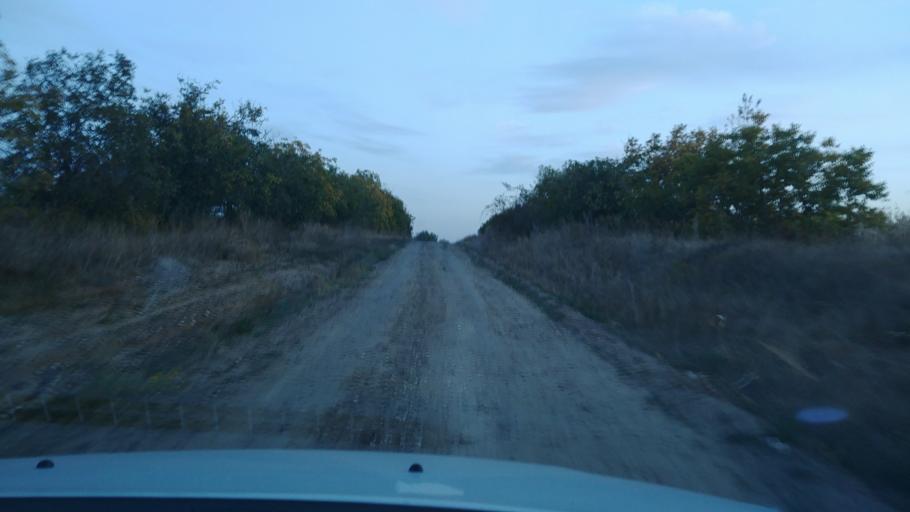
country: MD
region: Rezina
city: Saharna
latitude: 47.6833
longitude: 28.9078
